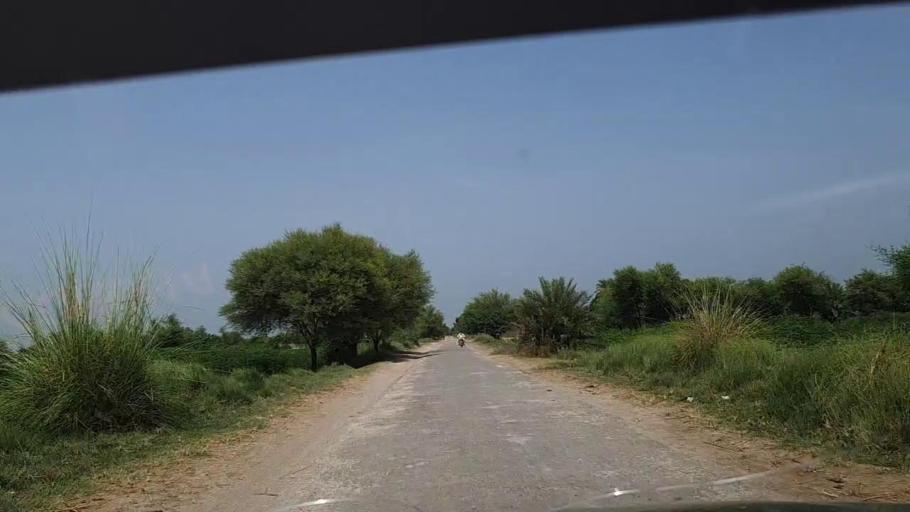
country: PK
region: Sindh
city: Khanpur
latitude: 27.8036
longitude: 69.4506
